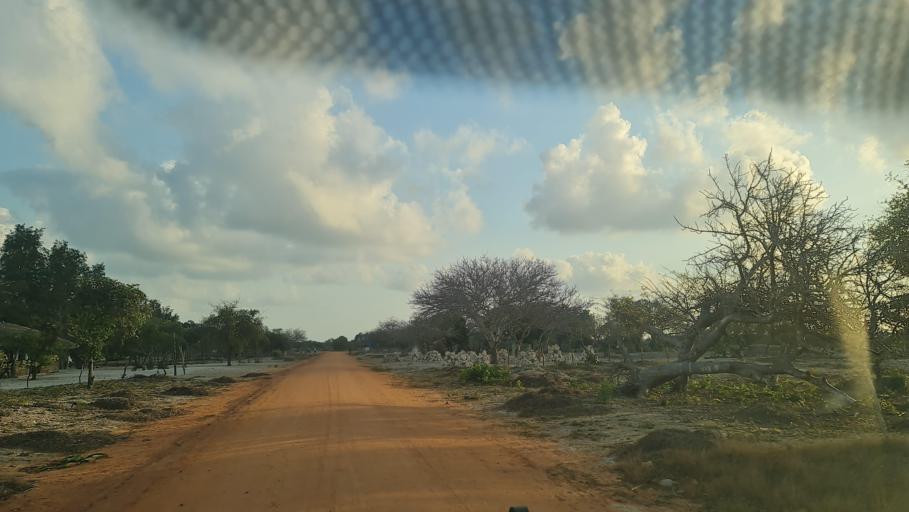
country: MZ
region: Nampula
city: Nacala
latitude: -14.7797
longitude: 40.8215
